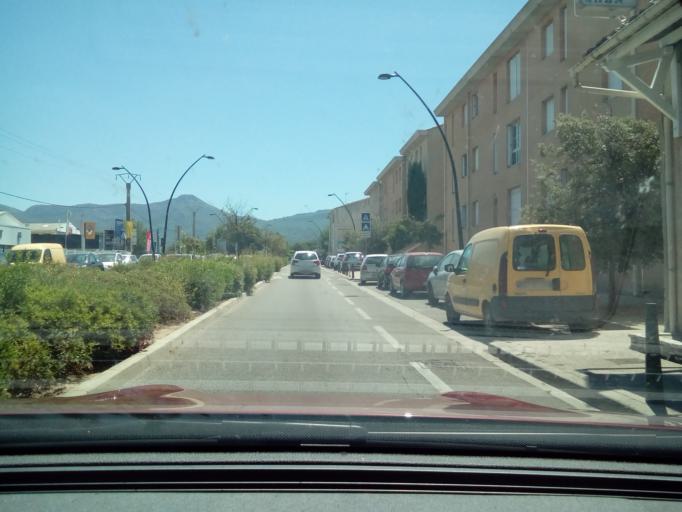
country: FR
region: Provence-Alpes-Cote d'Azur
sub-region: Departement des Bouches-du-Rhone
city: Trets
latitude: 43.4506
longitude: 5.6752
